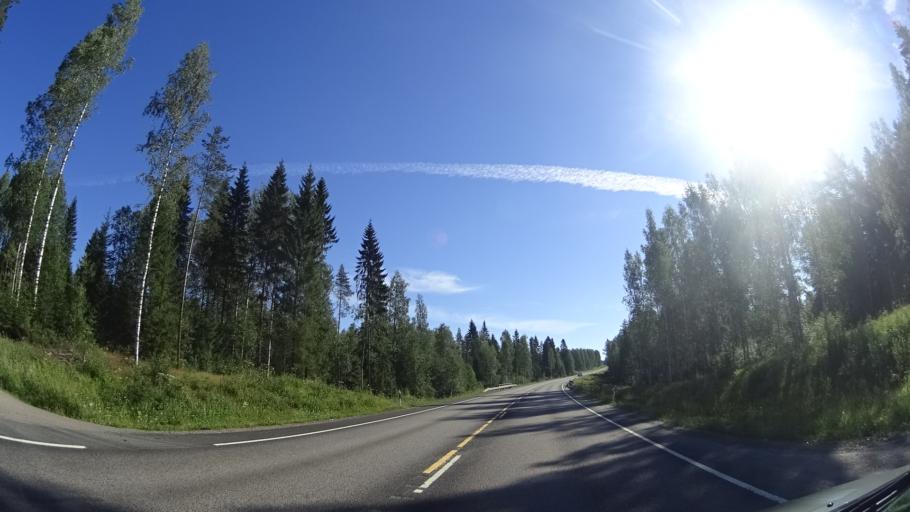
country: FI
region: Central Finland
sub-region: Jyvaeskylae
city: Petaejaevesi
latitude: 62.2676
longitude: 25.2888
